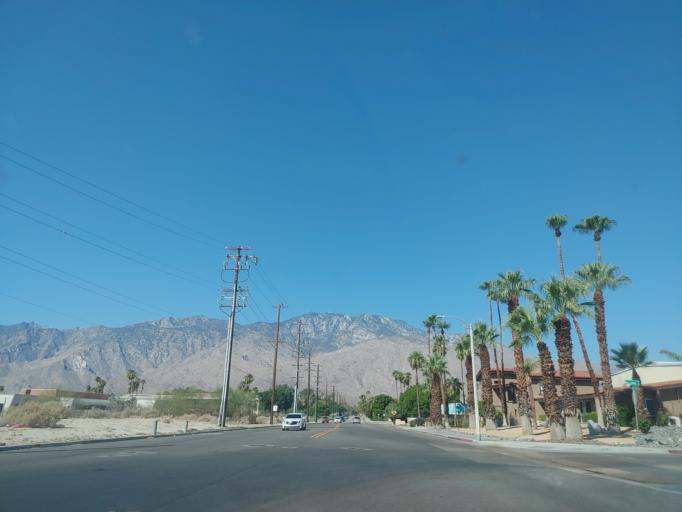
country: US
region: California
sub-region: Riverside County
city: Cathedral City
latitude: 33.8086
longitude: -116.4950
